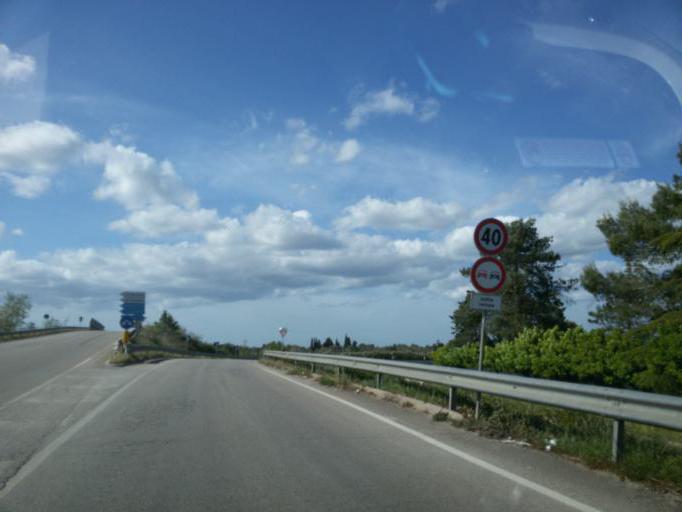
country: IT
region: Apulia
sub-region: Provincia di Brindisi
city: Mesagne
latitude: 40.5664
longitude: 17.7863
